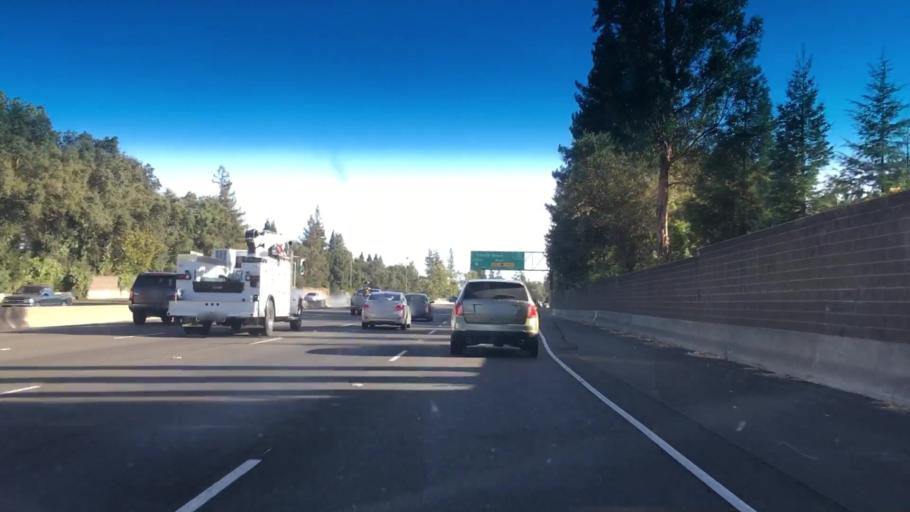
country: US
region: California
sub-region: Sacramento County
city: Parkway
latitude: 38.5045
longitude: -121.5193
